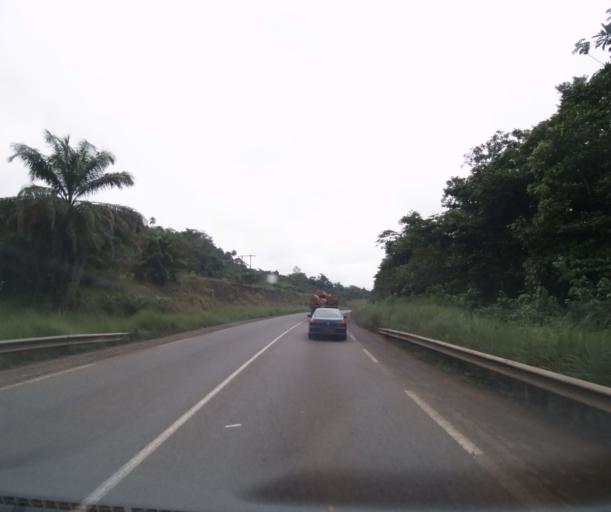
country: CM
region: Littoral
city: Edea
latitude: 3.7760
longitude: 10.1978
